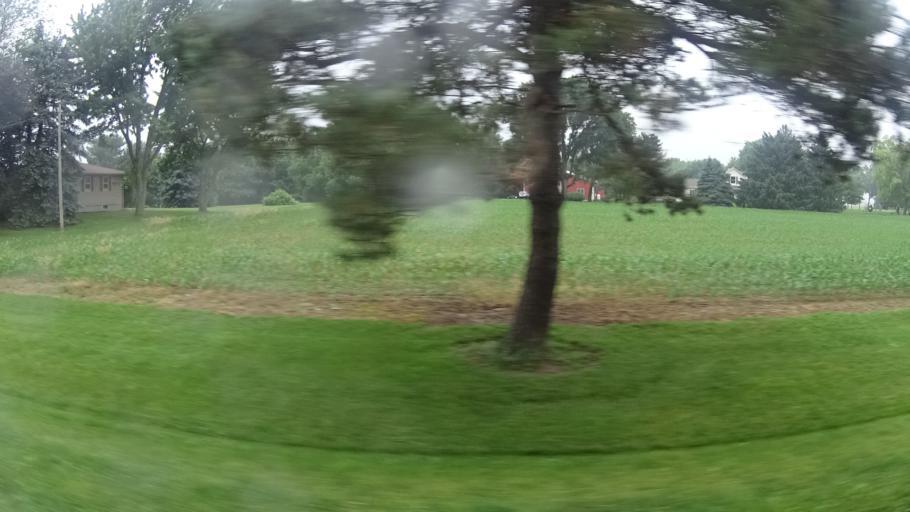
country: US
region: Ohio
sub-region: Huron County
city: Bellevue
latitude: 41.3624
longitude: -82.8217
